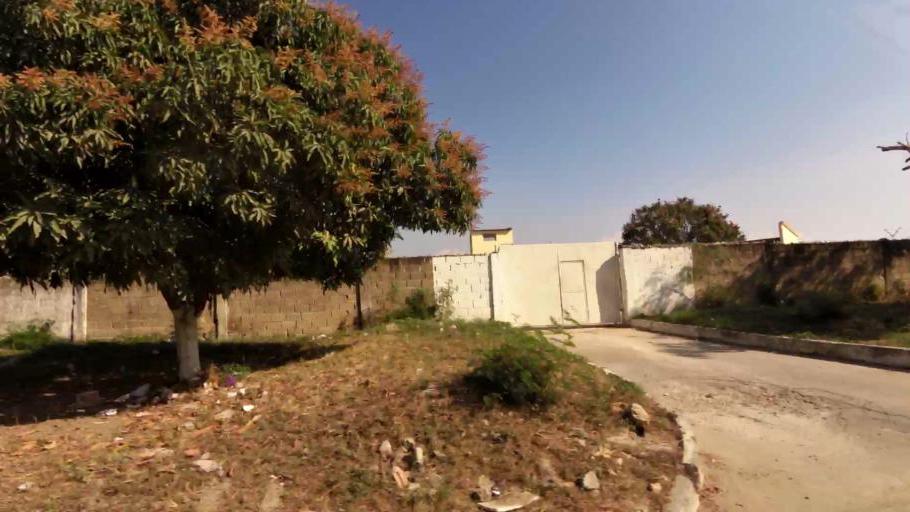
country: CO
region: Bolivar
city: Cartagena
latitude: 10.3847
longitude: -75.4770
